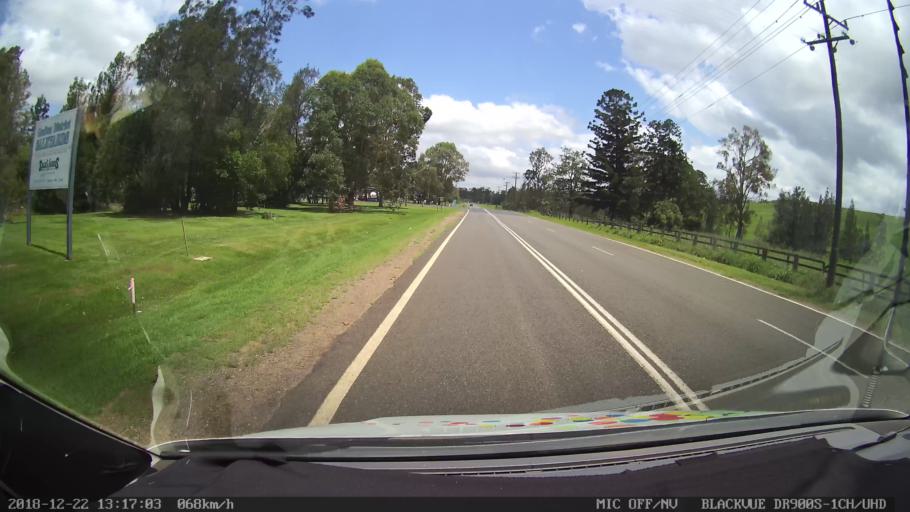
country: AU
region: New South Wales
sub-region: Clarence Valley
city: South Grafton
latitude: -29.7324
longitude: 152.9396
